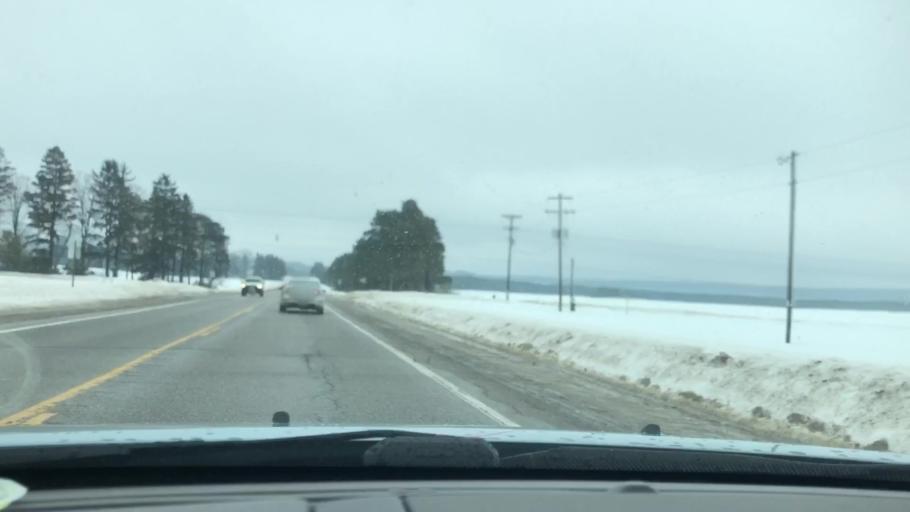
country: US
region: Michigan
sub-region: Charlevoix County
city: Boyne City
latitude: 45.0664
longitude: -84.8790
